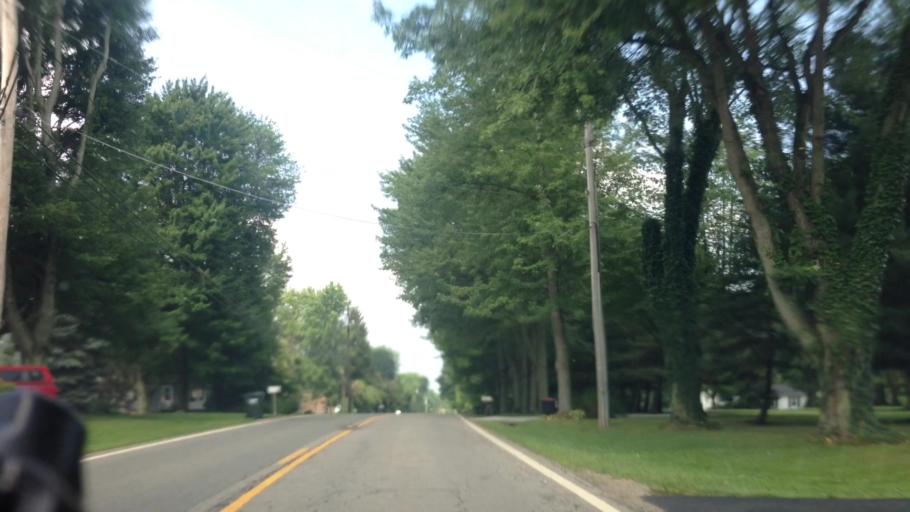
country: US
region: Ohio
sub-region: Stark County
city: Canal Fulton
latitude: 40.8439
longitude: -81.5896
